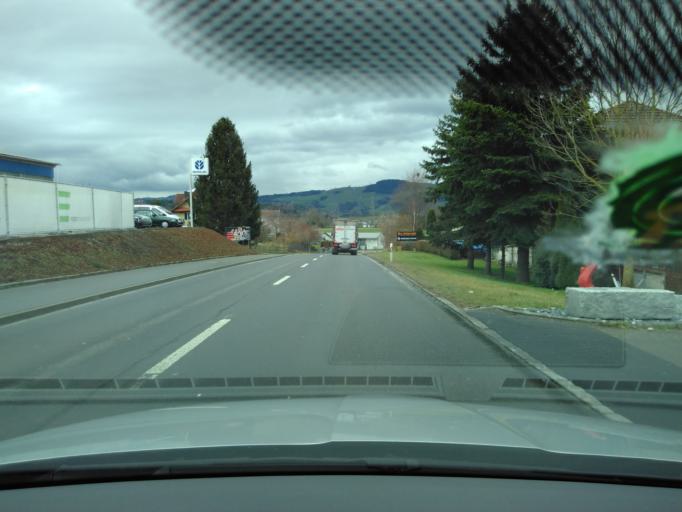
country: CH
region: Lucerne
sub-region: Hochdorf District
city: Inwil
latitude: 47.1274
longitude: 8.3285
